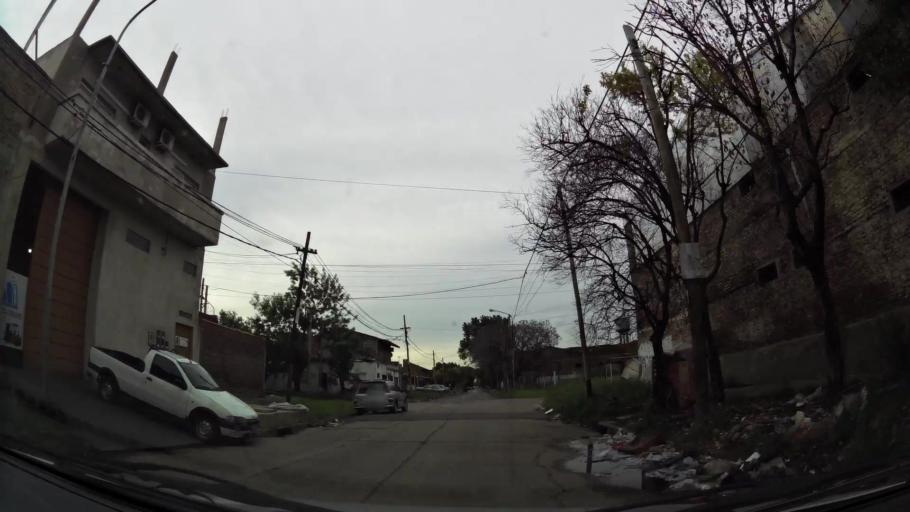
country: AR
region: Buenos Aires
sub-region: Partido de Lanus
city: Lanus
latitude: -34.7128
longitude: -58.3651
